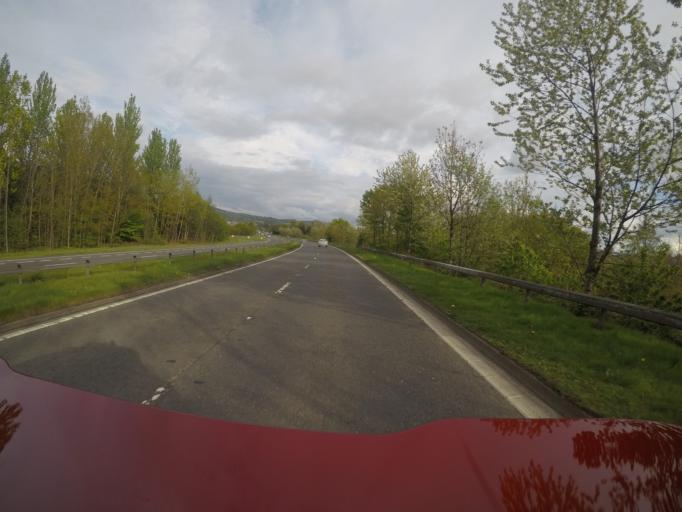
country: GB
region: Scotland
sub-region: West Dunbartonshire
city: Renton
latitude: 55.9618
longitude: -4.5842
